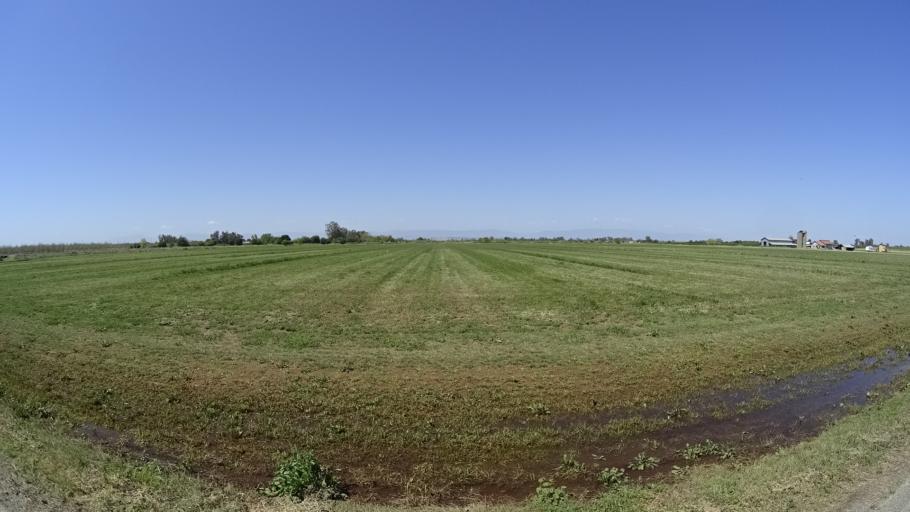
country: US
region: California
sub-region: Glenn County
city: Orland
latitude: 39.7739
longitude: -122.1690
